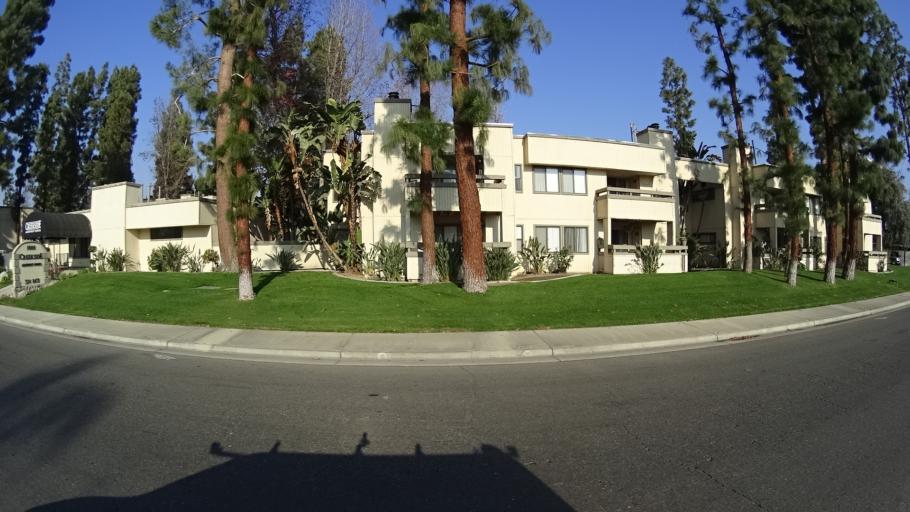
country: US
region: California
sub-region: Kern County
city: Bakersfield
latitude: 35.3628
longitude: -119.0636
